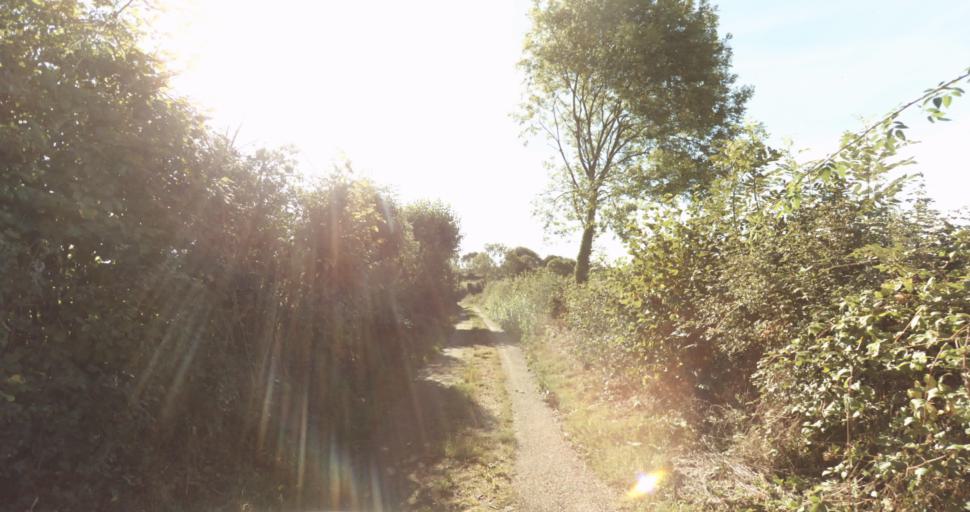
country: FR
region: Lower Normandy
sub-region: Departement de l'Orne
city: Vimoutiers
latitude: 48.9114
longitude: 0.1452
